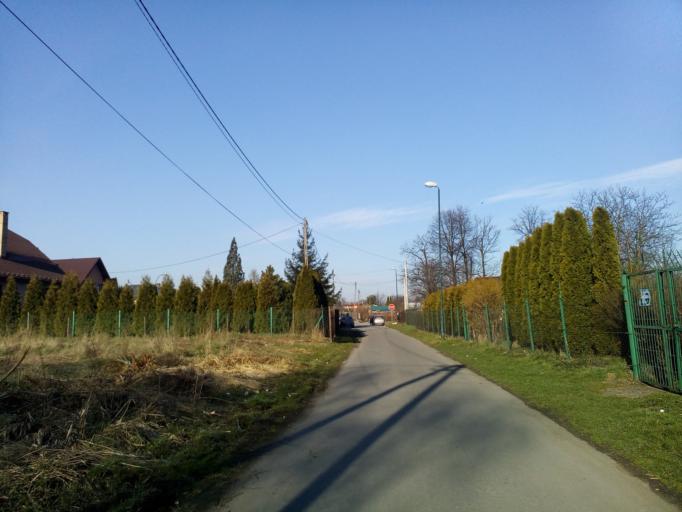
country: PL
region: Lesser Poland Voivodeship
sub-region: Powiat nowosadecki
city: Nowy Sacz
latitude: 49.6147
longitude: 20.6918
